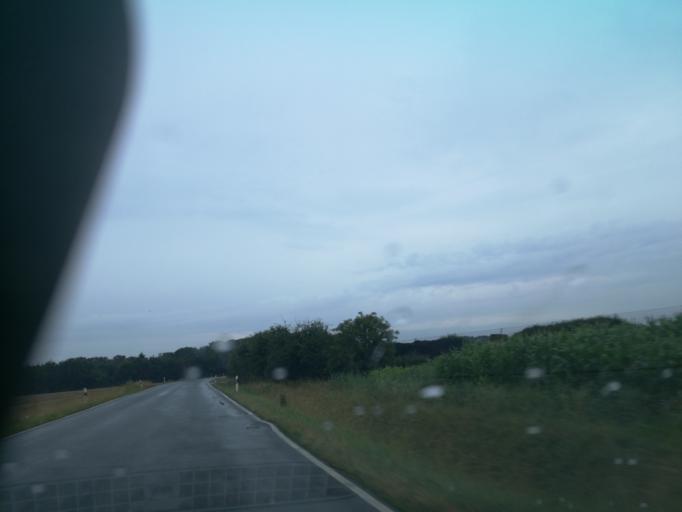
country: DE
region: Bavaria
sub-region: Regierungsbezirk Mittelfranken
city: Obermichelbach
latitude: 49.5329
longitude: 10.9456
